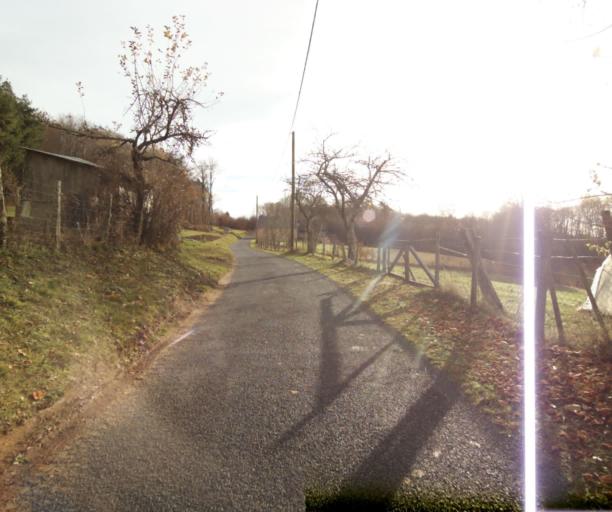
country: FR
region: Limousin
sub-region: Departement de la Correze
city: Sainte-Fortunade
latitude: 45.1864
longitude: 1.7891
